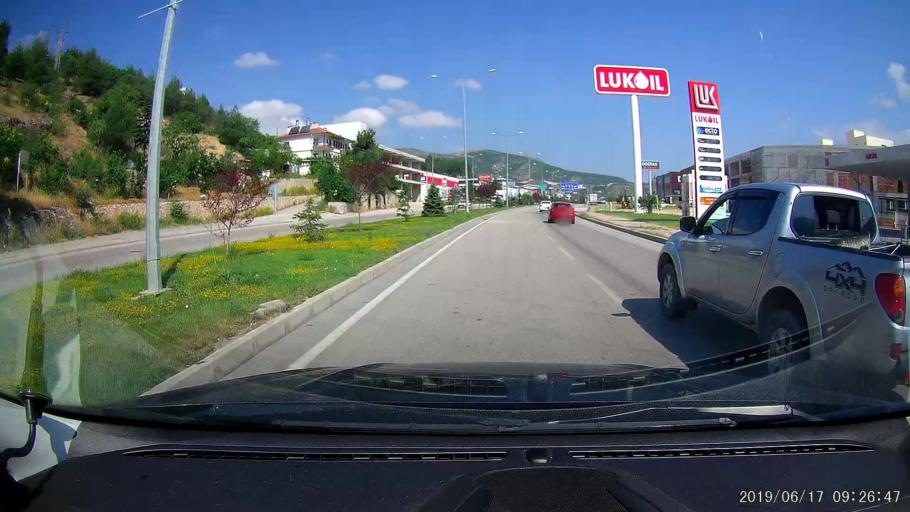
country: TR
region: Amasya
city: Amasya
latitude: 40.6713
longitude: 35.8319
